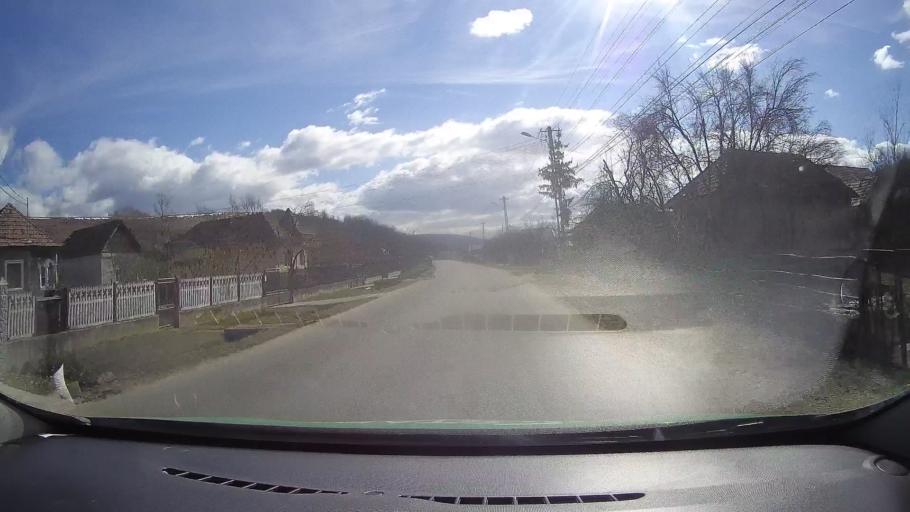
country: RO
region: Dambovita
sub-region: Comuna Vulcana-Pandele
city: Gura Vulcanei
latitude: 45.0362
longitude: 25.3915
